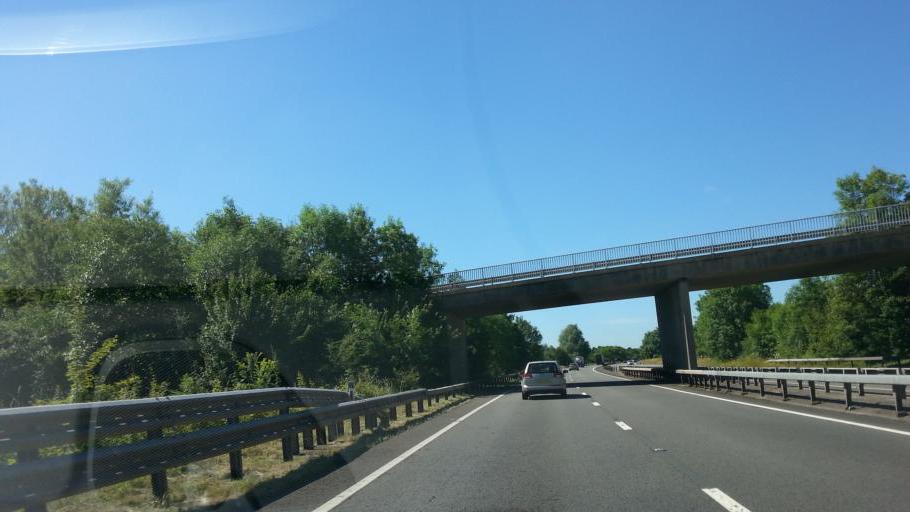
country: GB
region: Wales
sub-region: Monmouthshire
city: Llangwm
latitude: 51.7154
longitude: -2.8615
